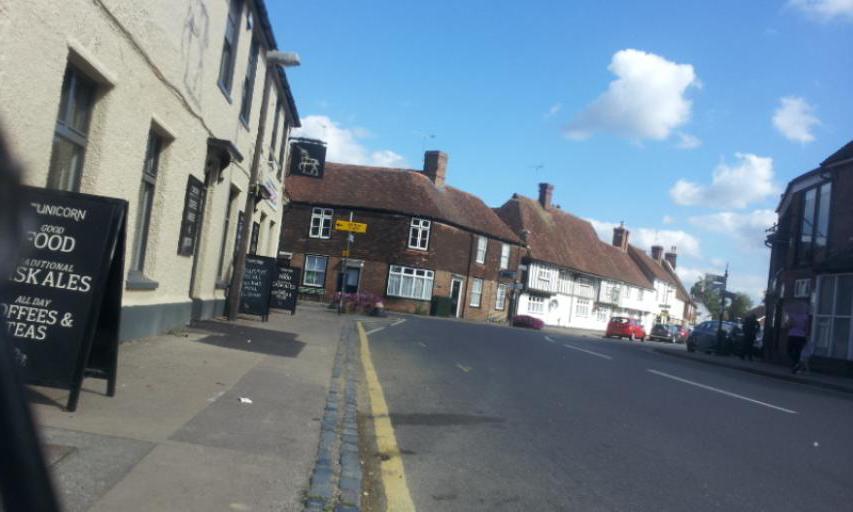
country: GB
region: England
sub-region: Kent
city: Marden
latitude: 51.1738
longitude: 0.4965
